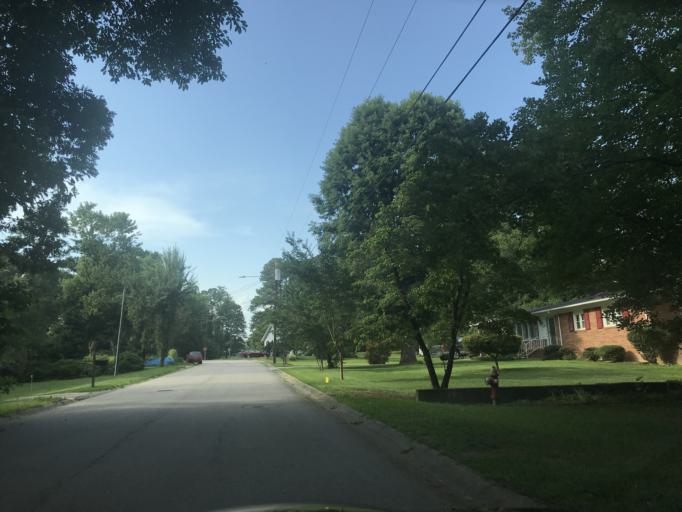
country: US
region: North Carolina
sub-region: Wake County
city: Raleigh
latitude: 35.8283
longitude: -78.5825
